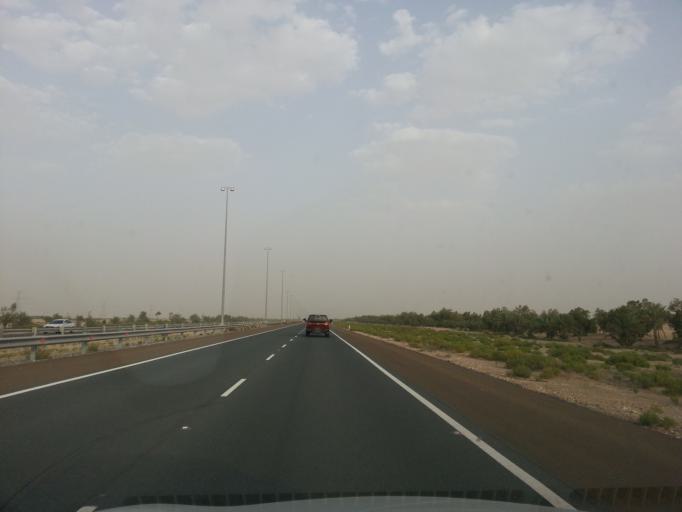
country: AE
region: Dubai
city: Dubai
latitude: 24.5962
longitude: 55.1366
